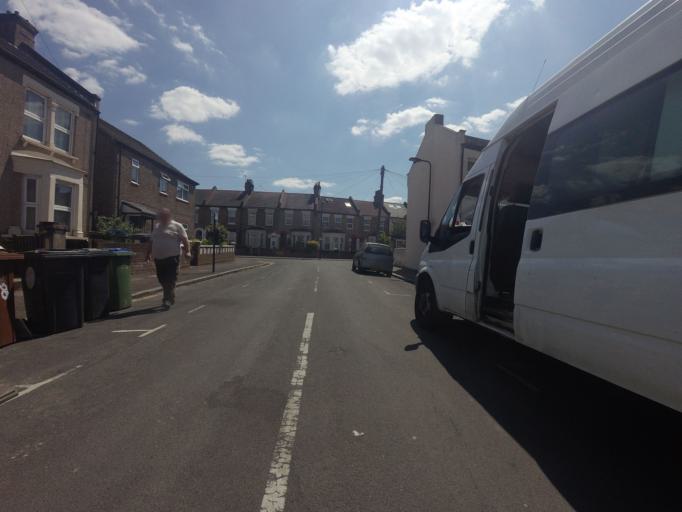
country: GB
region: England
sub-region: Greater London
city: East Ham
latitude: 51.5525
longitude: 0.0100
